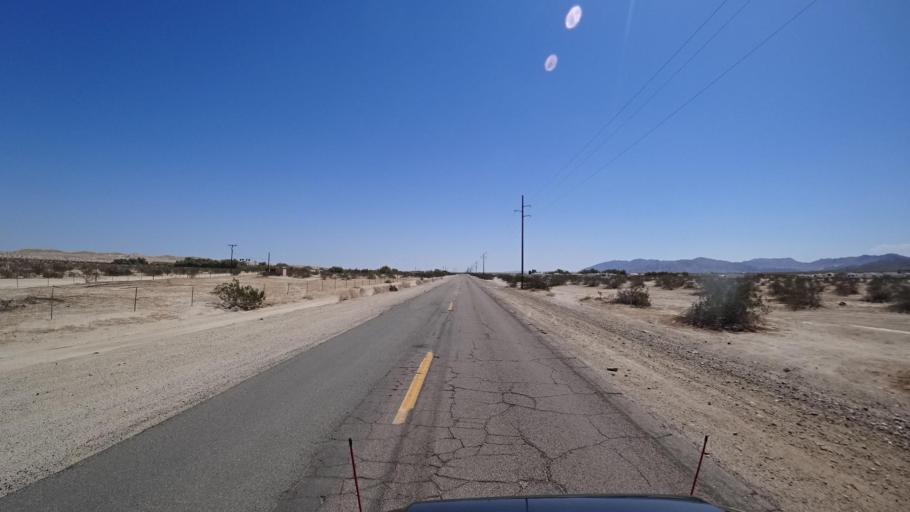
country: US
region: California
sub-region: Imperial County
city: Salton City
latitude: 33.1037
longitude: -116.1242
